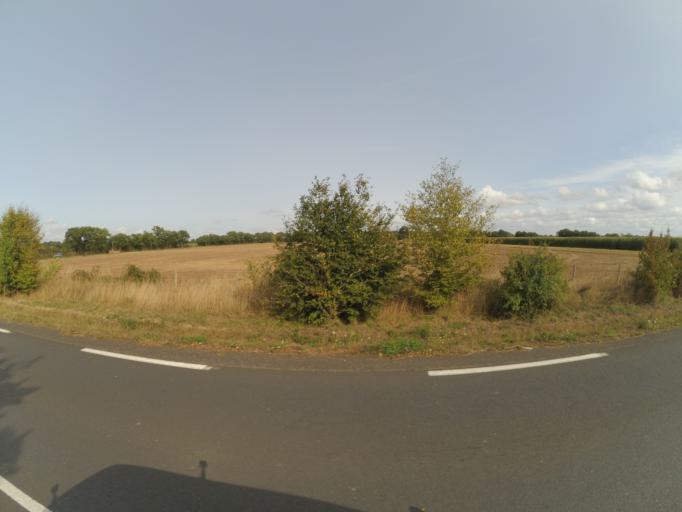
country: FR
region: Pays de la Loire
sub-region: Departement de la Vendee
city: Treize-Septiers
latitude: 46.9773
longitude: -1.2050
